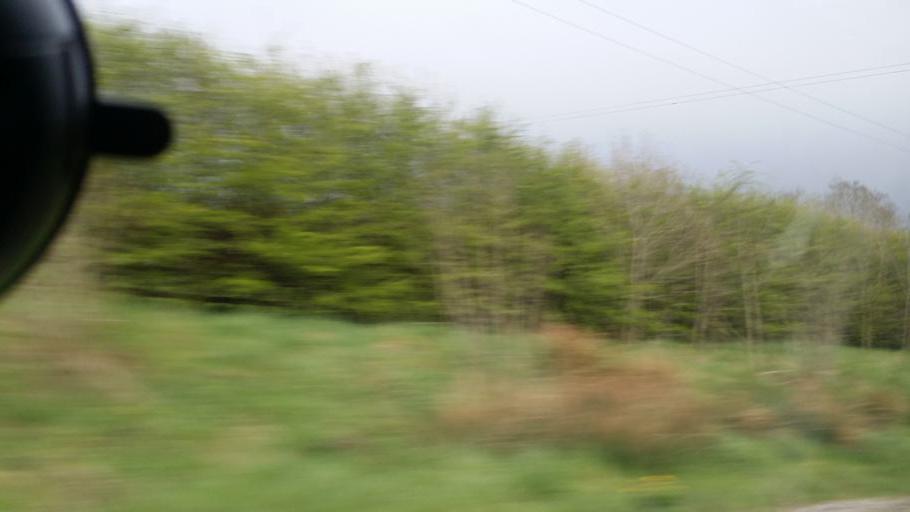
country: IE
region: Ulster
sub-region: An Cabhan
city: Virginia
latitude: 53.8653
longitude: -7.1142
